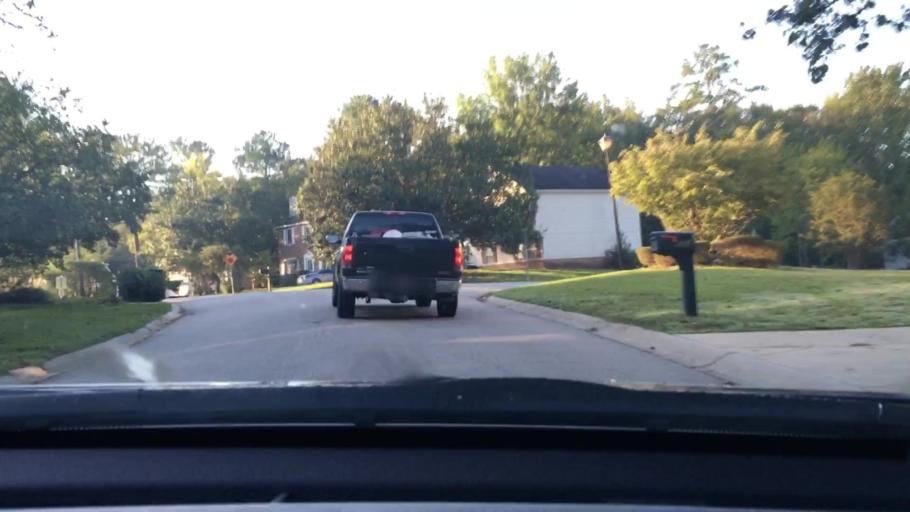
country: US
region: South Carolina
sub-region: Lexington County
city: Irmo
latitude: 34.1008
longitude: -81.1545
